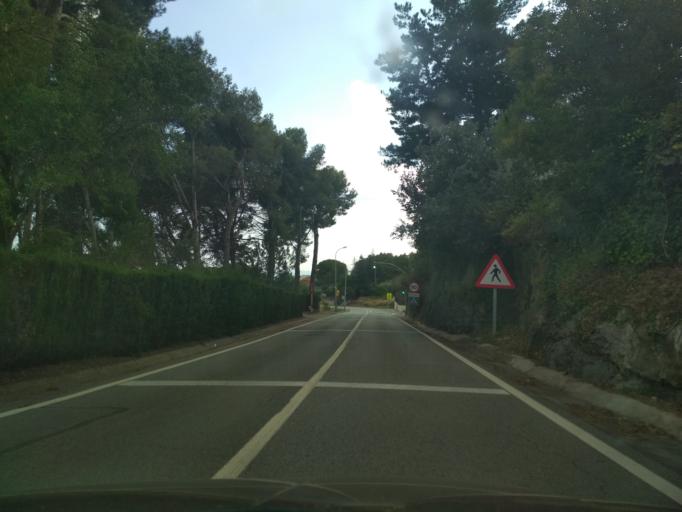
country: ES
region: Catalonia
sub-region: Provincia de Barcelona
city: Sant Feliu de Codines
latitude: 41.6923
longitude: 2.1703
